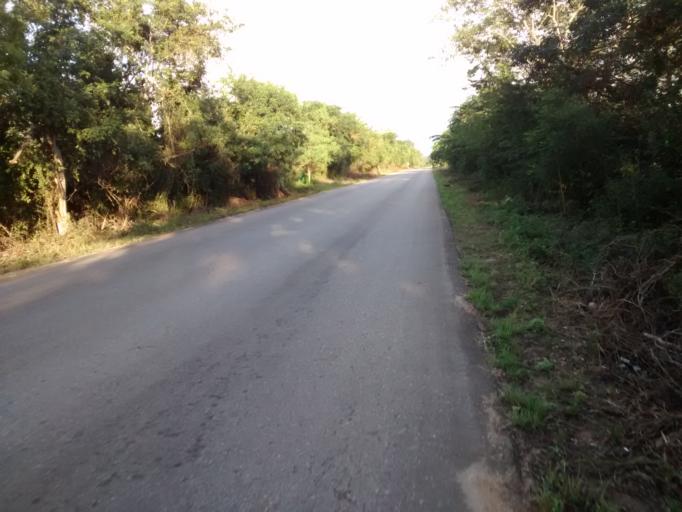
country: MX
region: Yucatan
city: Valladolid
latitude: 20.7311
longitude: -88.2112
